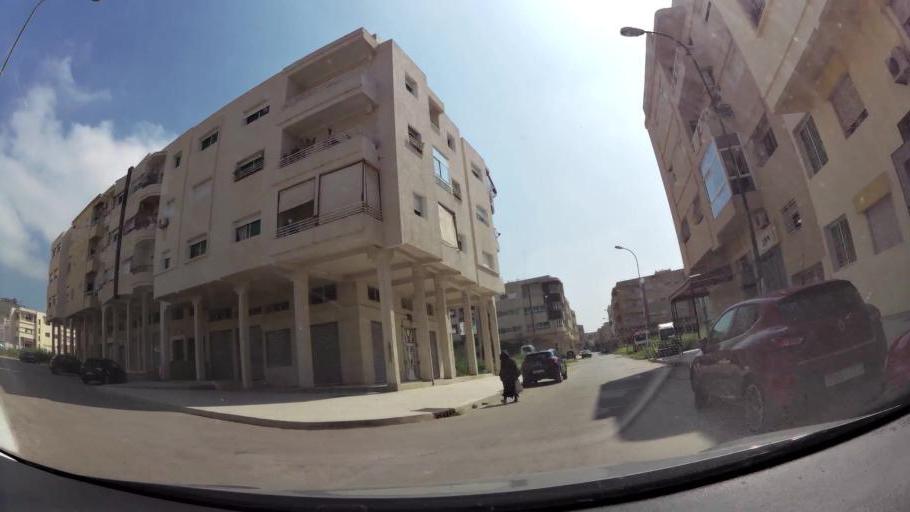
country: MA
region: Fes-Boulemane
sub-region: Fes
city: Fes
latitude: 34.0582
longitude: -5.0281
